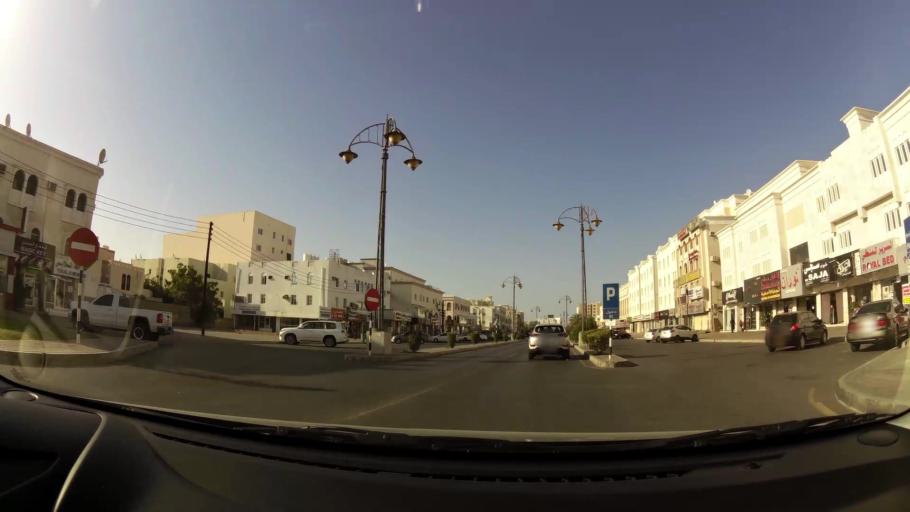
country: OM
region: Muhafazat Masqat
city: As Sib al Jadidah
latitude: 23.6346
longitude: 58.2001
